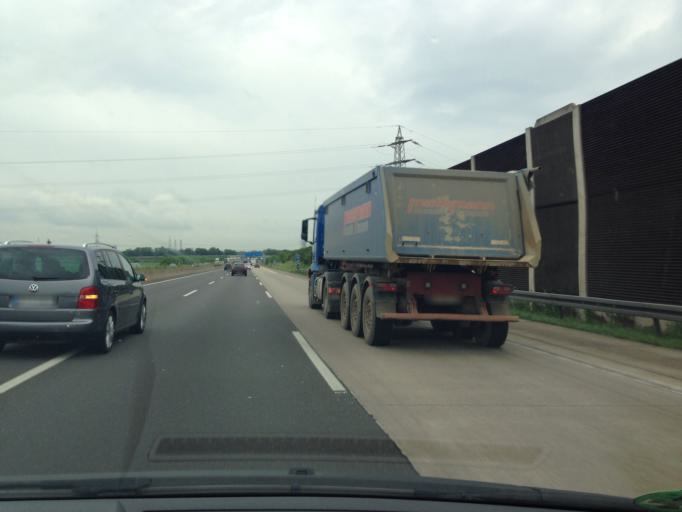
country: DE
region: North Rhine-Westphalia
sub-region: Regierungsbezirk Koln
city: Frechen
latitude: 50.9298
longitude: 6.8062
